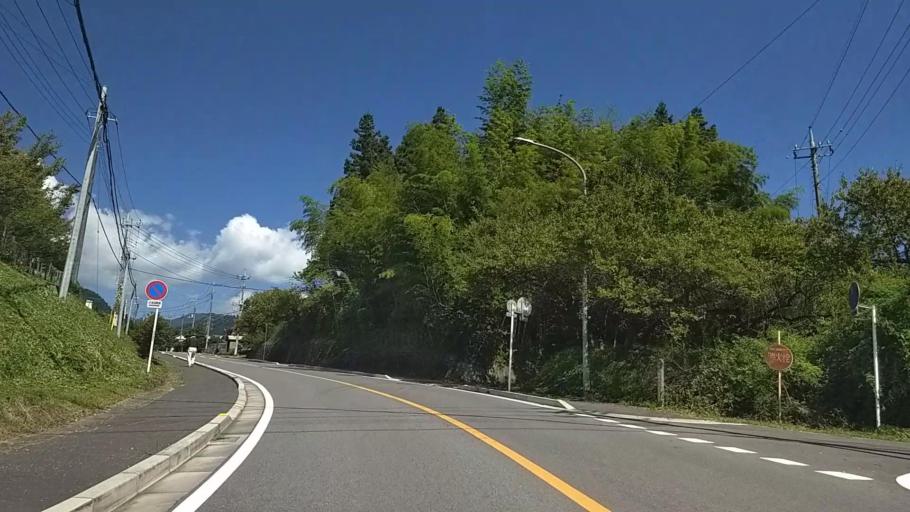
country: JP
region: Gunma
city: Annaka
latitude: 36.3401
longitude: 138.7271
